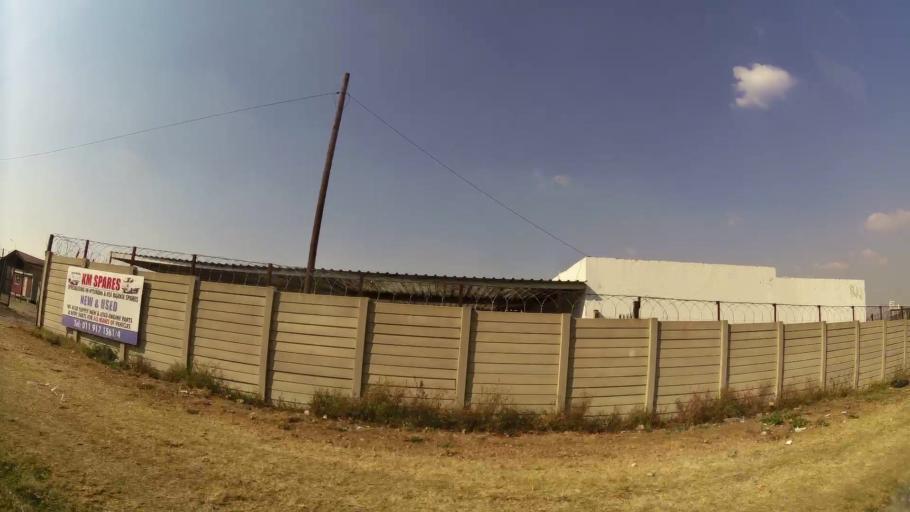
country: ZA
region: Gauteng
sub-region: Ekurhuleni Metropolitan Municipality
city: Boksburg
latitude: -26.2096
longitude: 28.2647
